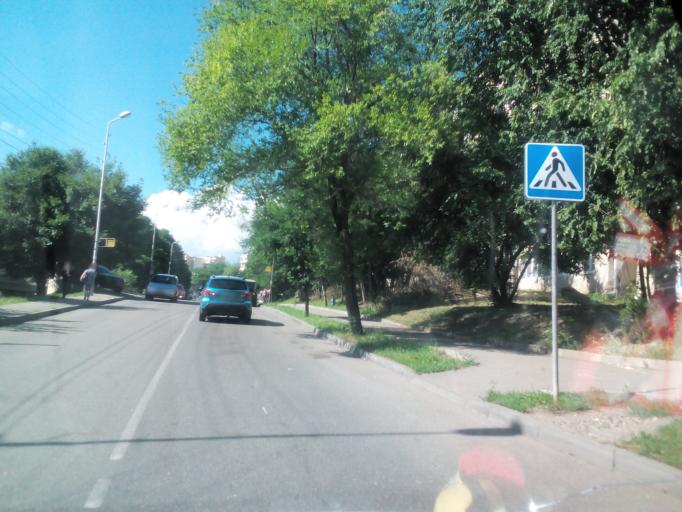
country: RU
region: Stavropol'skiy
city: Pyatigorsk
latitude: 44.0452
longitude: 43.0688
